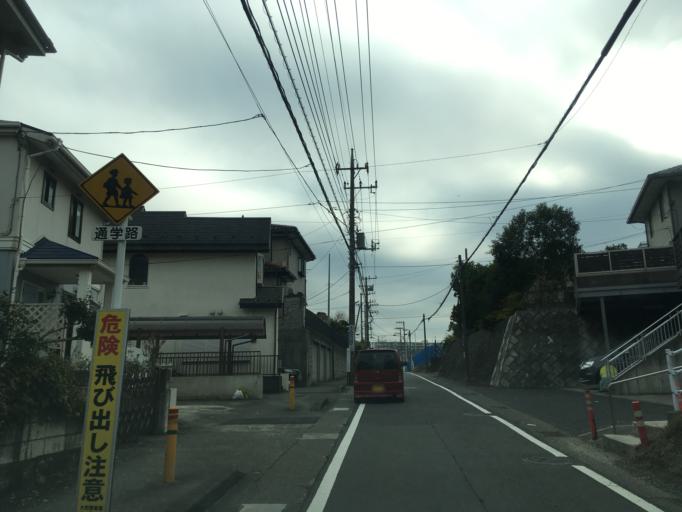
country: JP
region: Kanagawa
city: Minami-rinkan
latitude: 35.5087
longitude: 139.4638
